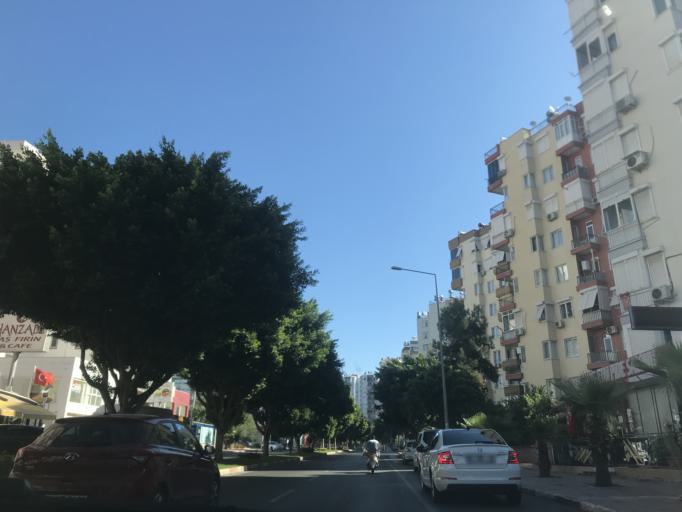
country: TR
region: Antalya
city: Antalya
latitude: 36.8960
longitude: 30.6290
